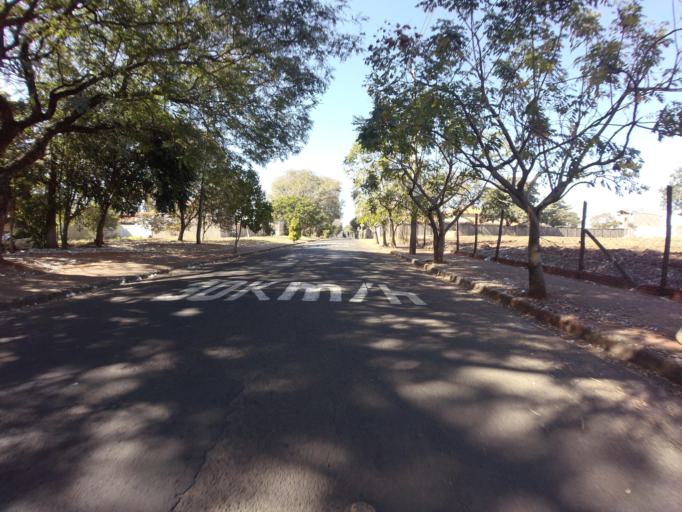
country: BR
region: Sao Paulo
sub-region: Piracicaba
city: Piracicaba
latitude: -22.7690
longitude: -47.5895
